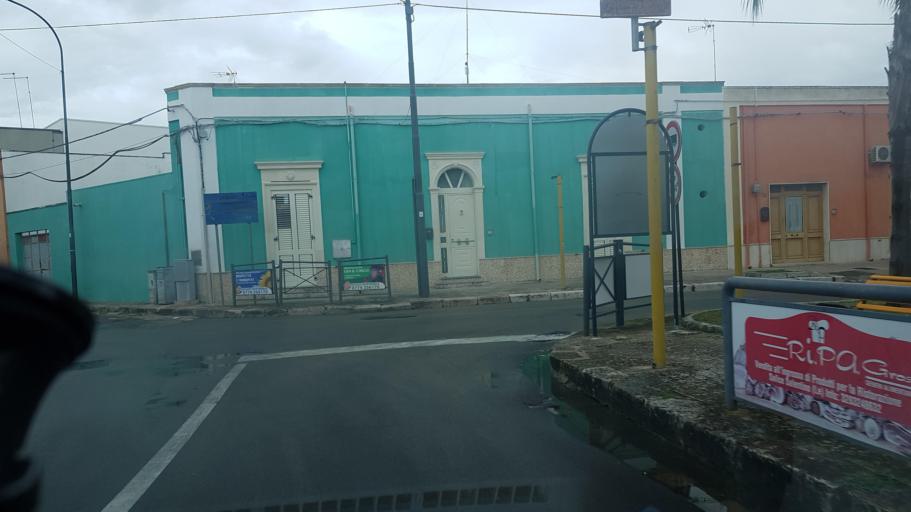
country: IT
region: Apulia
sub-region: Provincia di Lecce
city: Salice Salentino
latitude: 40.3873
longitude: 17.9600
